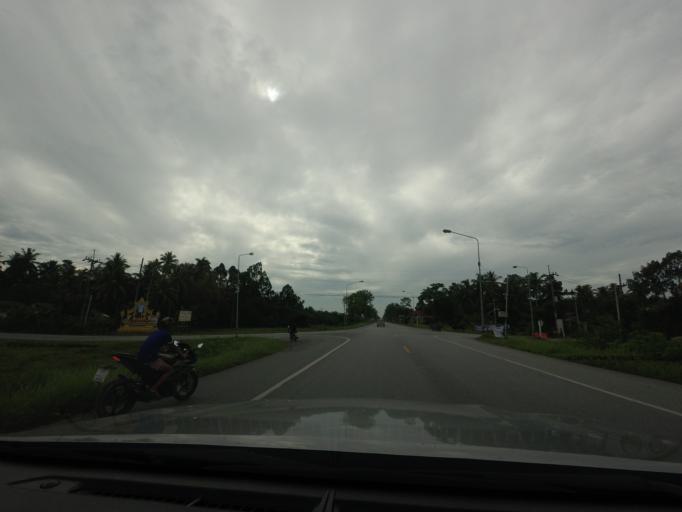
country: TH
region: Nakhon Si Thammarat
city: Phra Phrom
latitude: 8.3230
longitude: 99.9459
